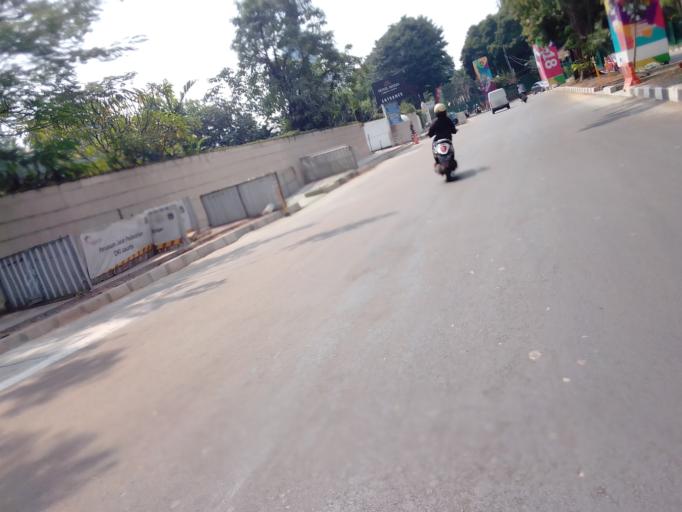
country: ID
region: Jakarta Raya
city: Jakarta
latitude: -6.2145
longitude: 106.7979
